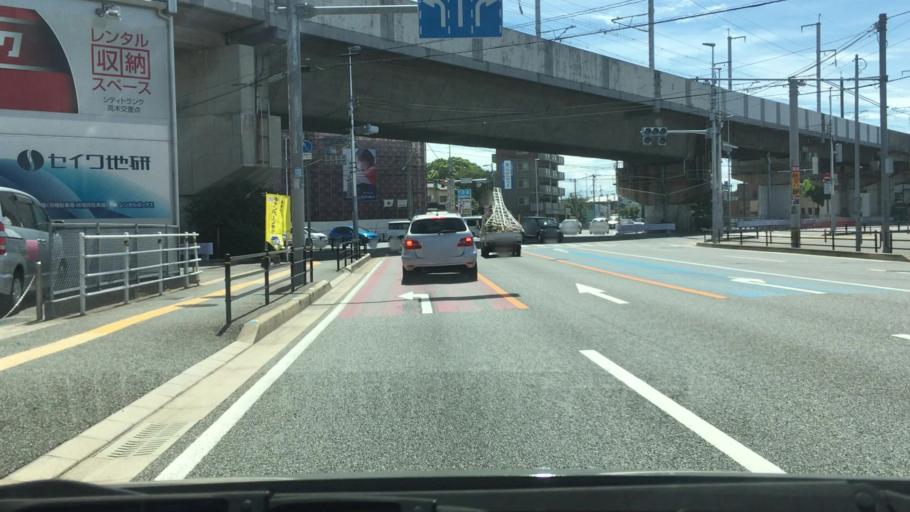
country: JP
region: Fukuoka
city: Fukuoka-shi
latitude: 33.5616
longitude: 130.4353
